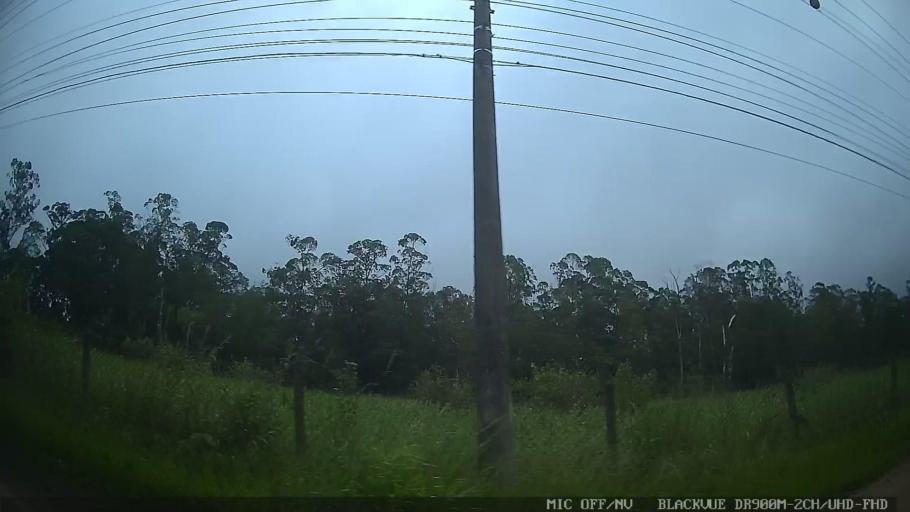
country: BR
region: Sao Paulo
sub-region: Mogi das Cruzes
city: Mogi das Cruzes
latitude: -23.5235
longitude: -46.1516
